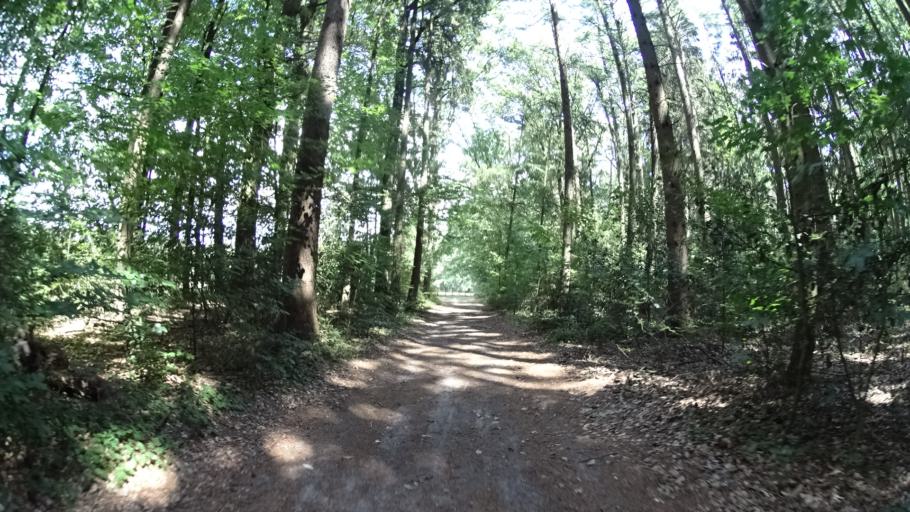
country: DE
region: Lower Saxony
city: Undeloh
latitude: 53.2305
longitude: 9.9212
